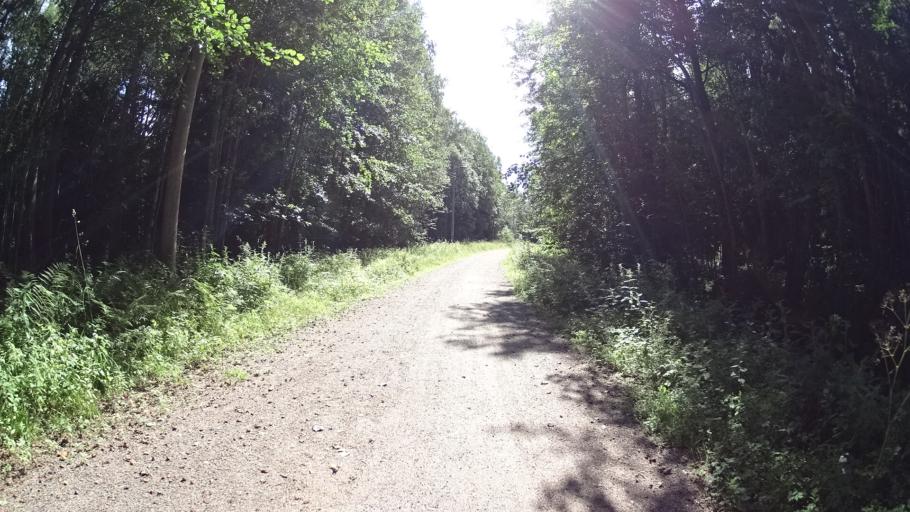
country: FI
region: Uusimaa
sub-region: Helsinki
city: Kirkkonummi
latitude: 60.1106
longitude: 24.4605
